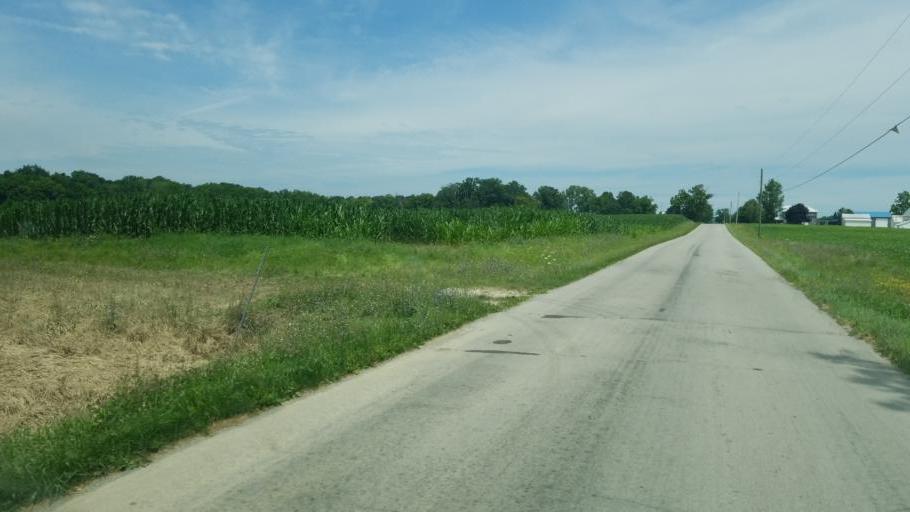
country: US
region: Ohio
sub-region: Wyandot County
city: Upper Sandusky
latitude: 40.8692
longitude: -83.2227
